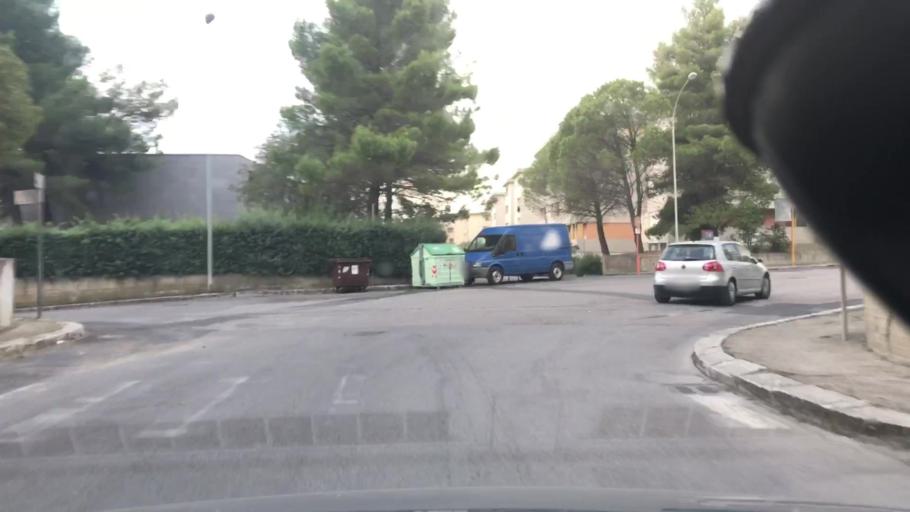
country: IT
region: Basilicate
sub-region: Provincia di Matera
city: Matera
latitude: 40.6863
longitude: 16.5855
